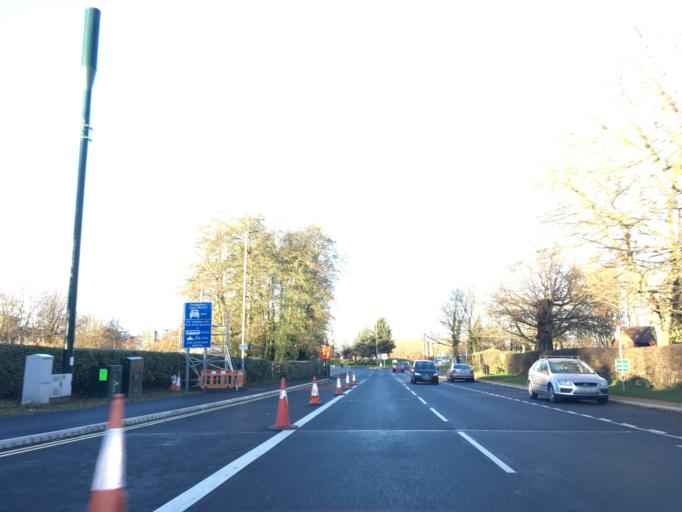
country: GB
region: England
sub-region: South Gloucestershire
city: Stoke Gifford
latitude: 51.4985
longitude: -2.5439
